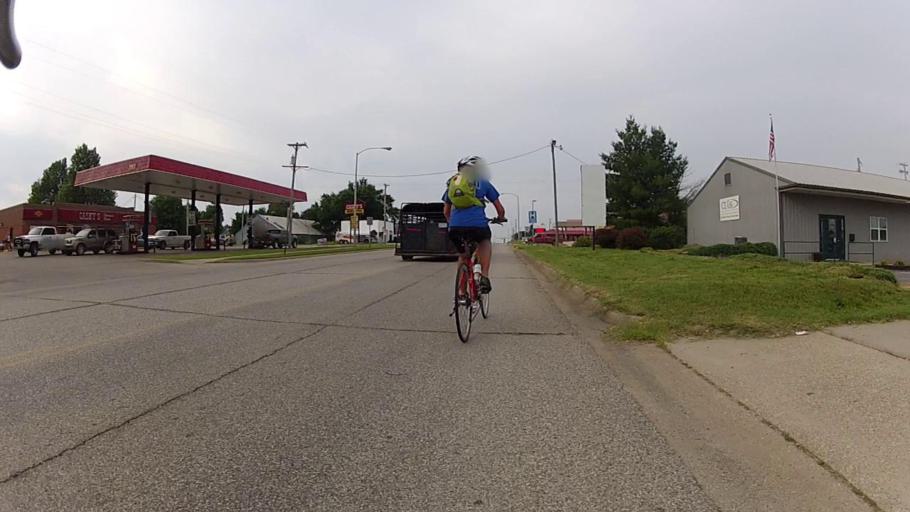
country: US
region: Kansas
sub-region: Cherokee County
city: Columbus
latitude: 37.1734
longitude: -94.8318
